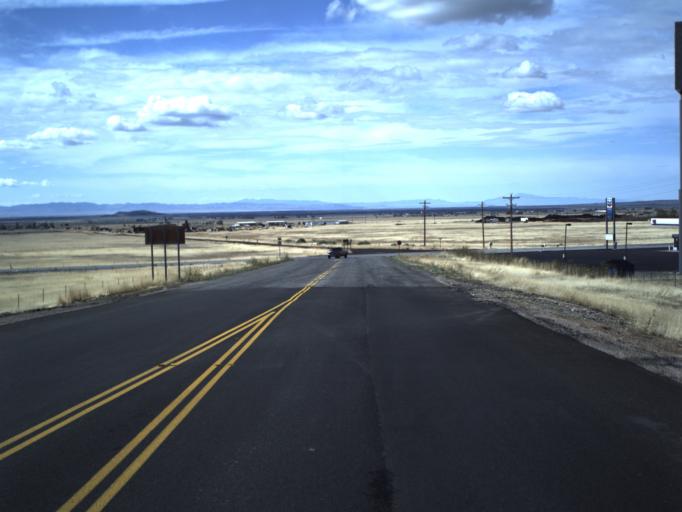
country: US
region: Utah
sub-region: Millard County
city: Fillmore
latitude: 38.9493
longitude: -112.3516
